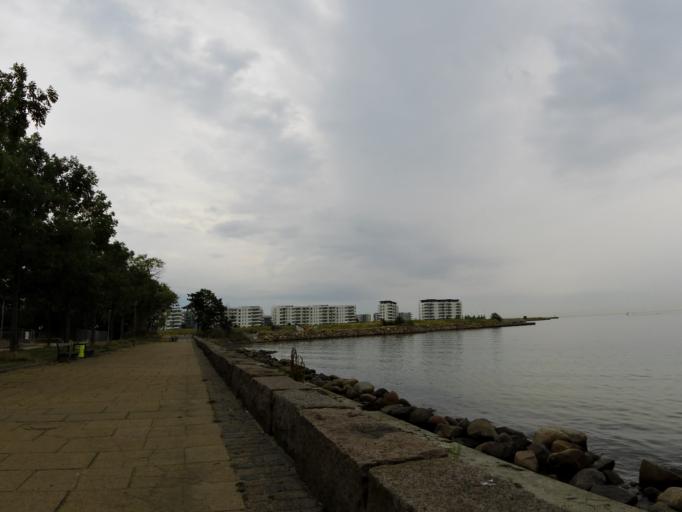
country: DK
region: Capital Region
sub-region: Gentofte Kommune
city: Charlottenlund
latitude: 55.7207
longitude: 12.5831
